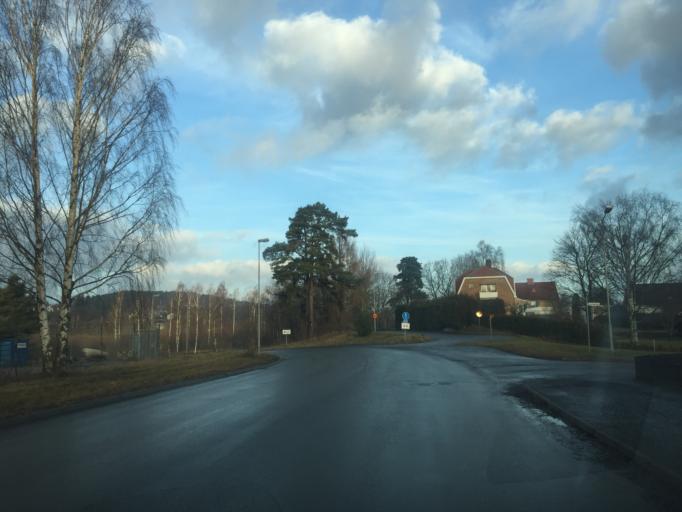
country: SE
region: Joenkoeping
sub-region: Jonkopings Kommun
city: Jonkoping
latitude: 57.7596
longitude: 14.1434
